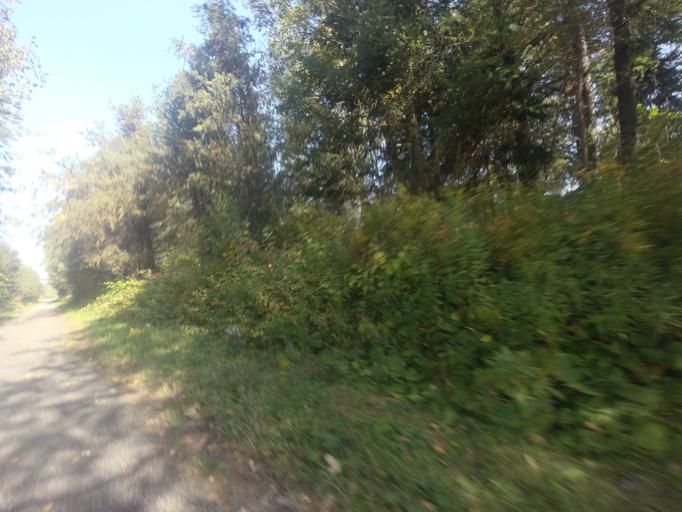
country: CA
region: Quebec
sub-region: Laurentides
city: Mont-Laurier
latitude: 46.5220
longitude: -75.4465
